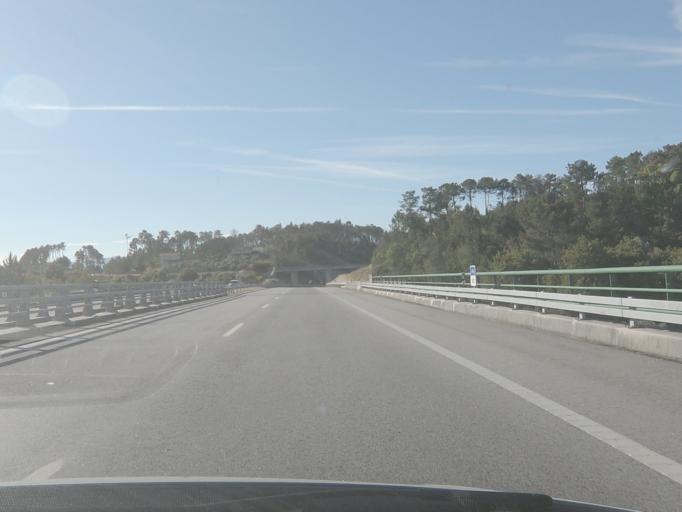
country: PT
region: Viseu
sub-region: Viseu
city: Campo
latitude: 40.7742
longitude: -7.9255
